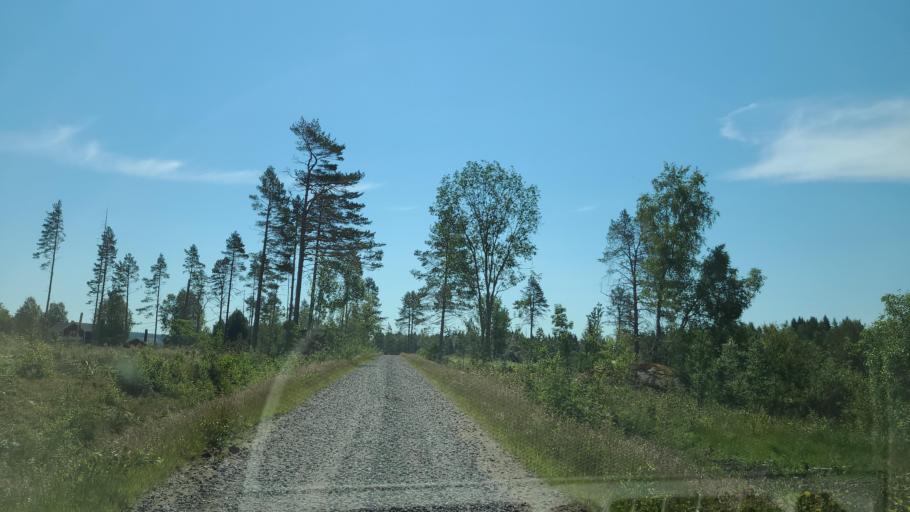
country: SE
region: Vaesterbotten
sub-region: Robertsfors Kommun
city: Robertsfors
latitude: 64.0892
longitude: 20.8382
